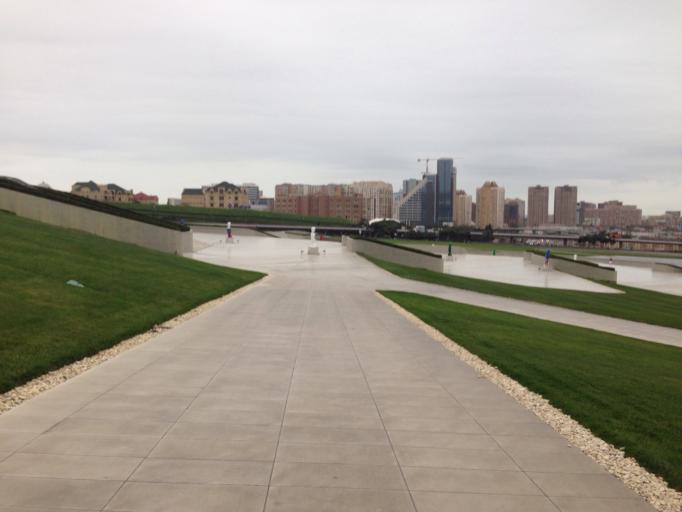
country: AZ
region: Baki
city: Baku
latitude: 40.3954
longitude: 49.8659
